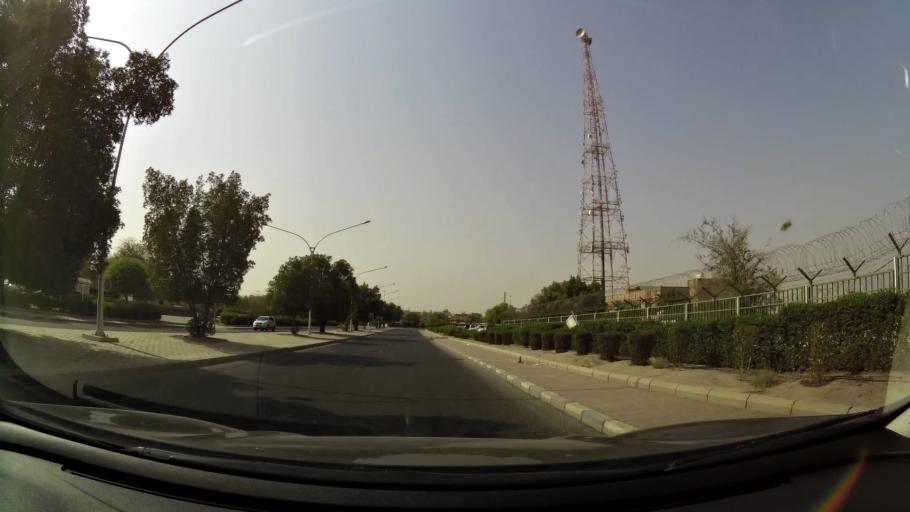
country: KW
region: Al Asimah
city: Ar Rabiyah
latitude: 29.2878
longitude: 47.8841
